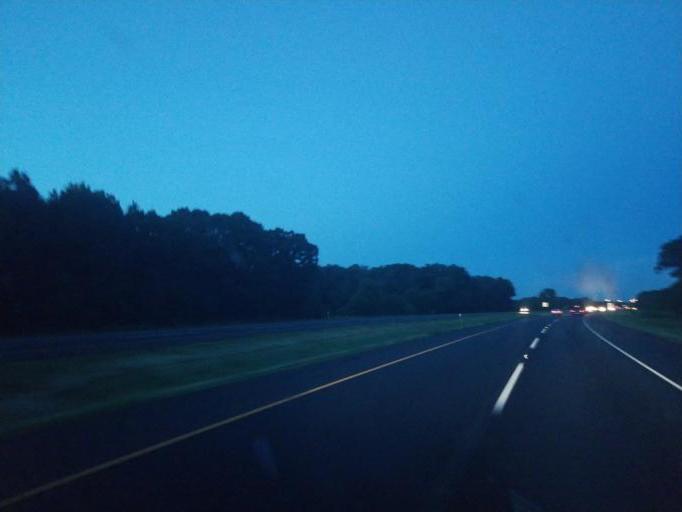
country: US
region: Indiana
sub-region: Elkhart County
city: Simonton Lake
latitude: 41.7330
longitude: -86.0406
